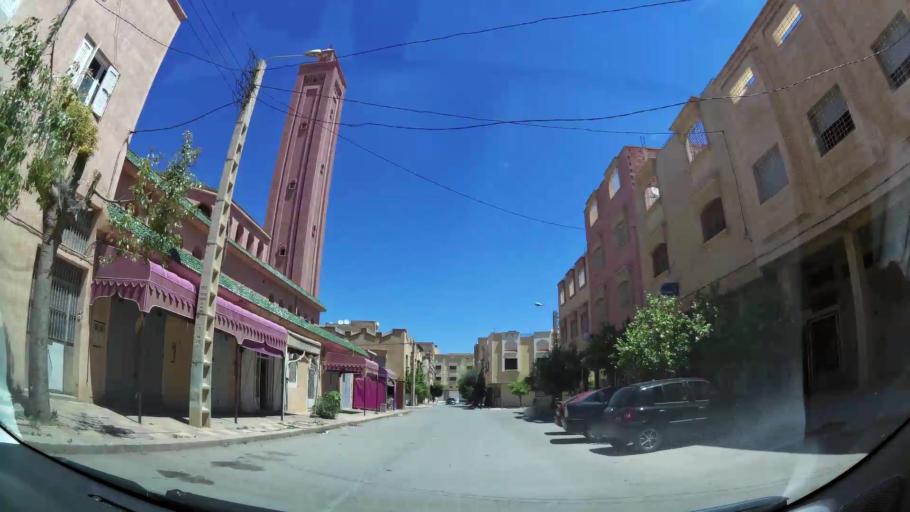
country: MA
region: Oriental
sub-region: Oujda-Angad
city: Oujda
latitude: 34.6714
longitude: -1.8896
